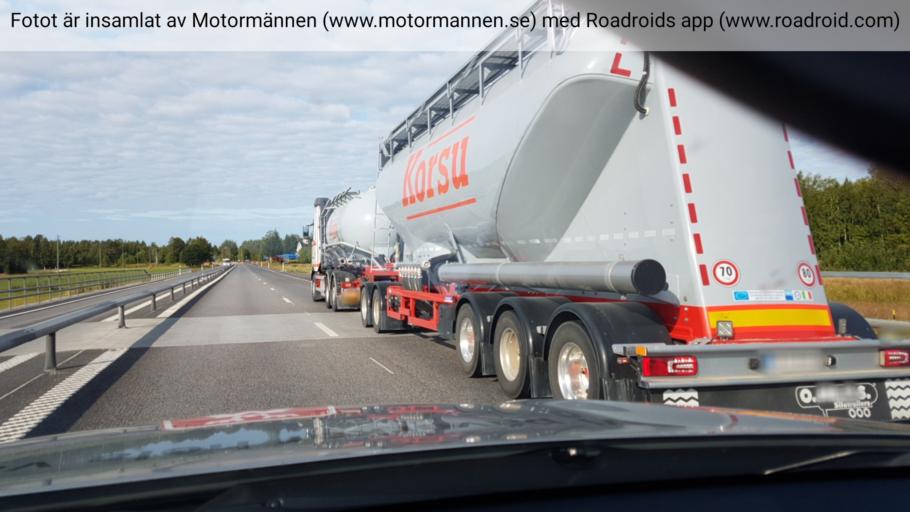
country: SE
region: Norrbotten
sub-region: Pitea Kommun
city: Norrfjarden
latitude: 65.4092
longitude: 21.5040
